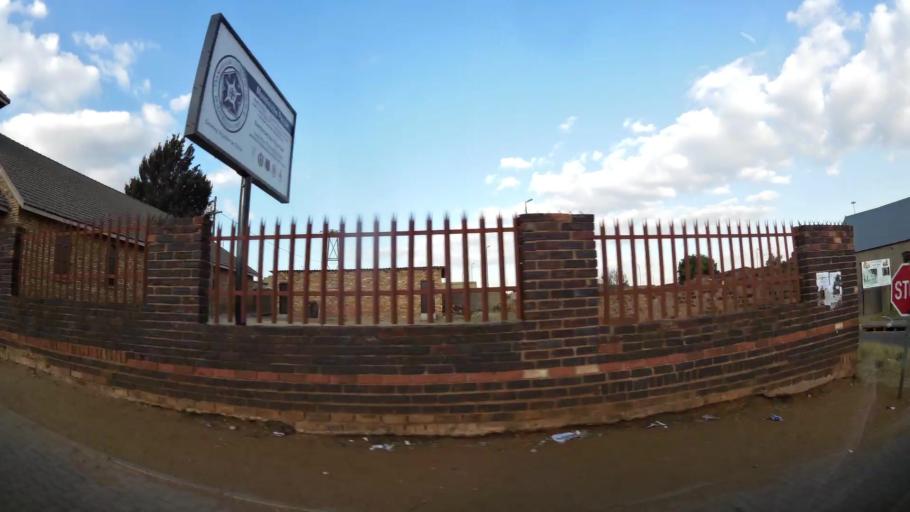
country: ZA
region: Gauteng
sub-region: West Rand District Municipality
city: Krugersdorp
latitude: -26.0740
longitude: 27.7585
